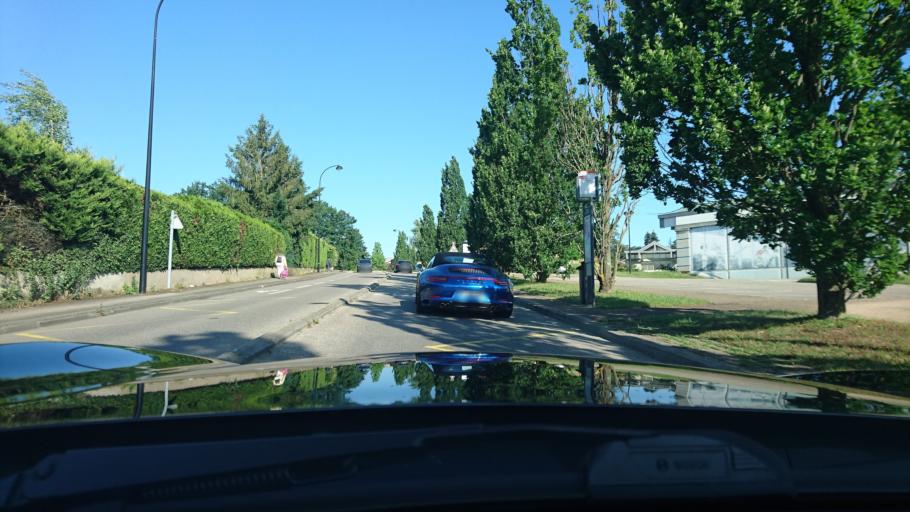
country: FR
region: Rhone-Alpes
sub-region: Departement du Rhone
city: Chaponost
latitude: 45.7078
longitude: 4.7484
